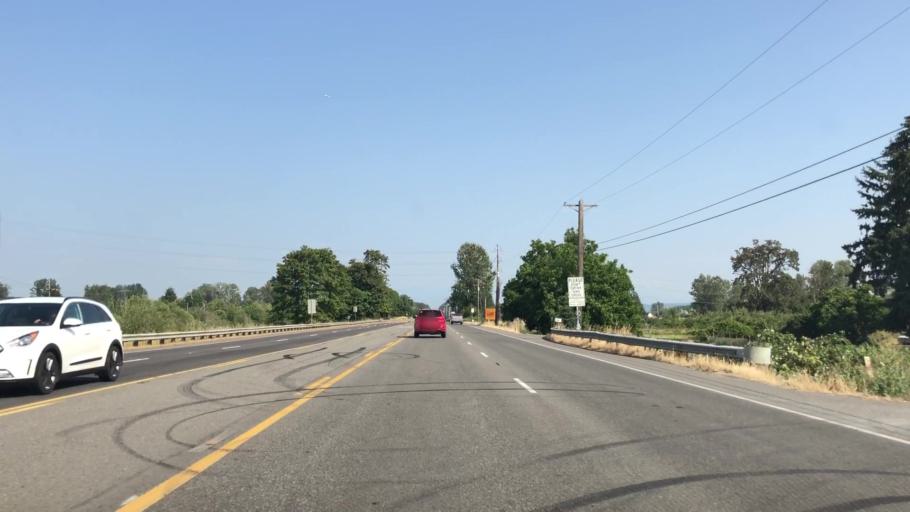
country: US
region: Washington
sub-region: Pierce County
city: Fife
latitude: 47.2281
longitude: -122.3730
